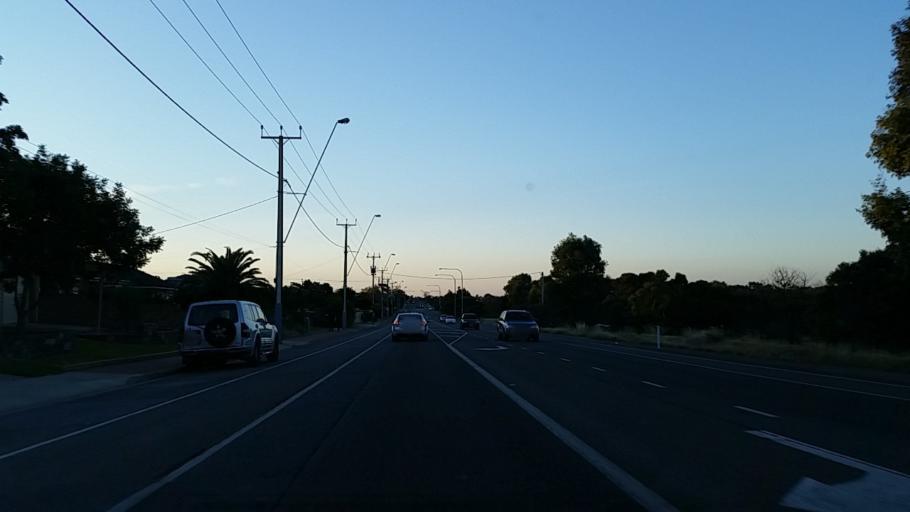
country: AU
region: South Australia
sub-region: Adelaide
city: Port Noarlunga
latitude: -35.1632
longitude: 138.4753
